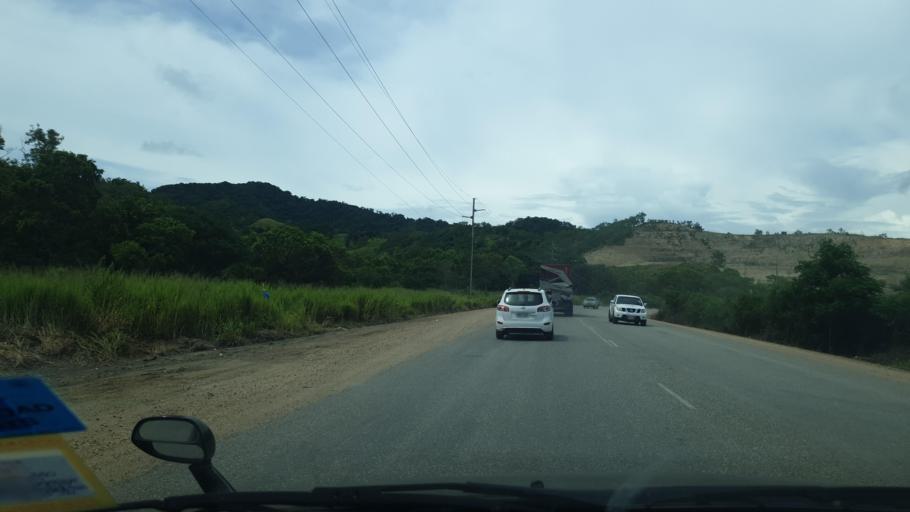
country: PG
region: National Capital
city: Port Moresby
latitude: -9.4167
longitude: 147.0998
